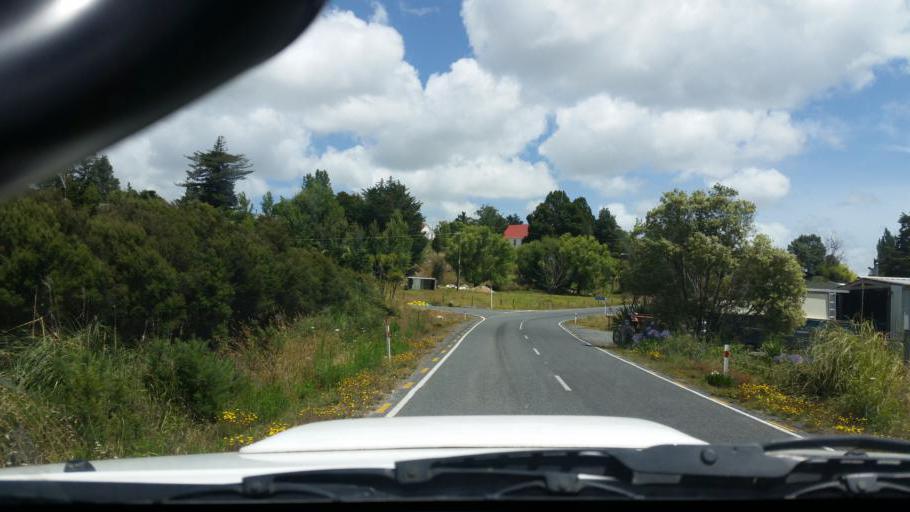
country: NZ
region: Northland
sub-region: Whangarei
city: Ruakaka
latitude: -36.0951
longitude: 174.2429
